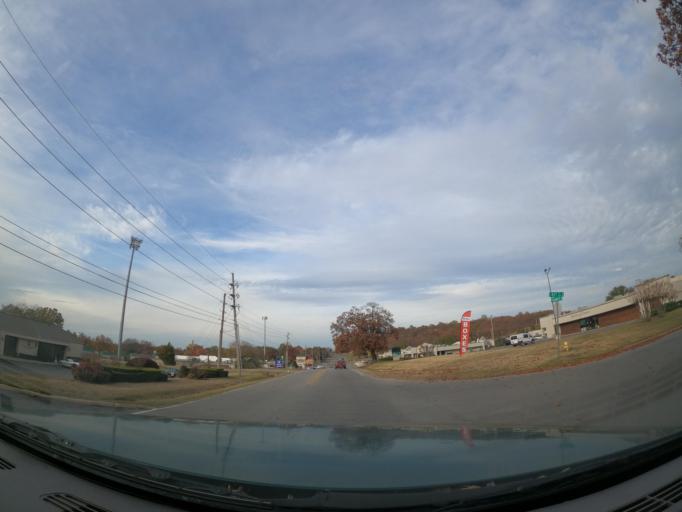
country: US
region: Oklahoma
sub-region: Tulsa County
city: Jenks
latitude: 36.0436
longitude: -95.9400
